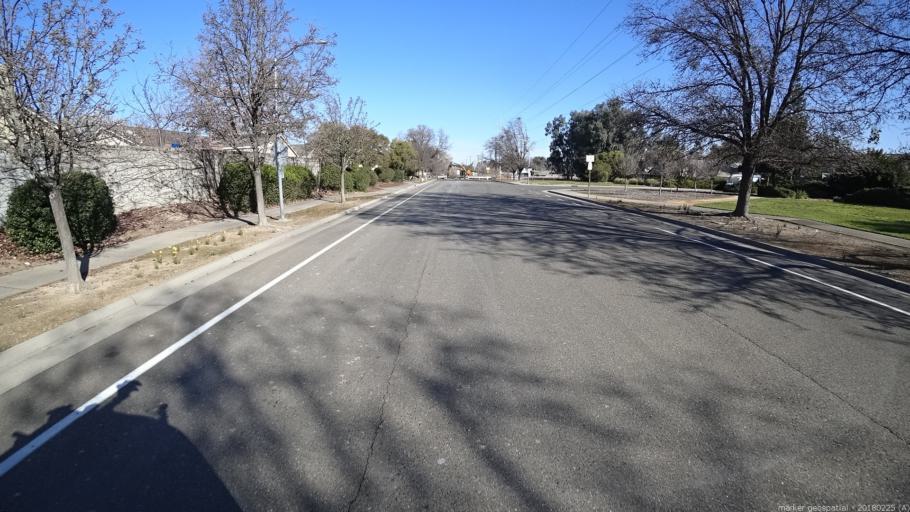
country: US
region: California
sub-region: Sacramento County
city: Antelope
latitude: 38.7245
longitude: -121.3465
